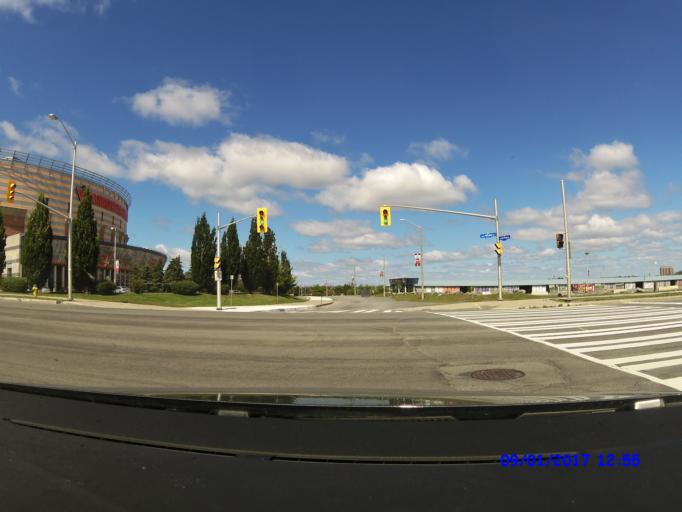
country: CA
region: Ontario
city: Bells Corners
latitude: 45.2962
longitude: -75.9248
